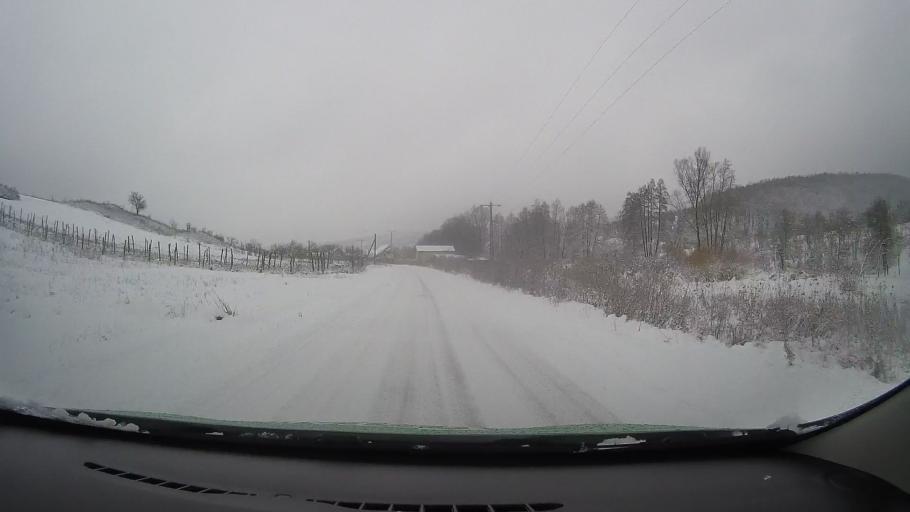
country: RO
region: Hunedoara
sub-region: Comuna Carjiti
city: Carjiti
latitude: 45.8318
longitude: 22.8417
